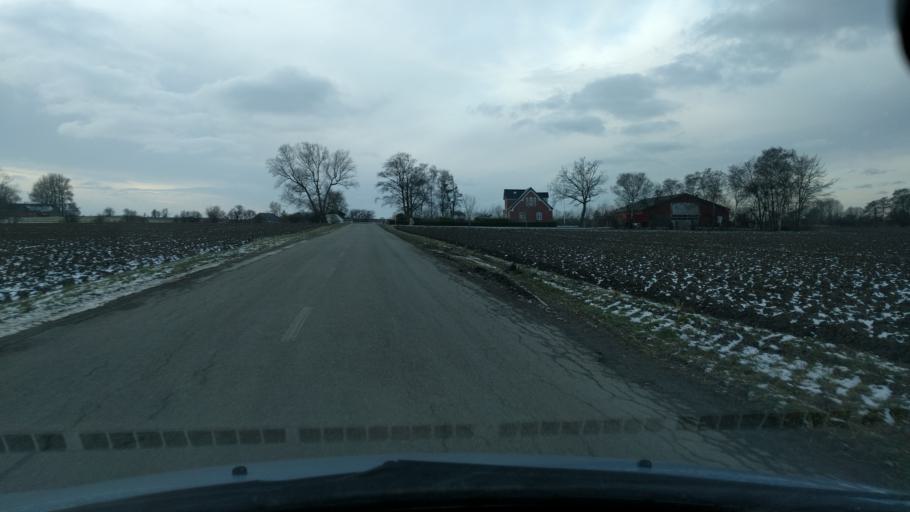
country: DK
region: Zealand
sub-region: Guldborgsund Kommune
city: Stubbekobing
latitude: 54.8225
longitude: 12.0930
